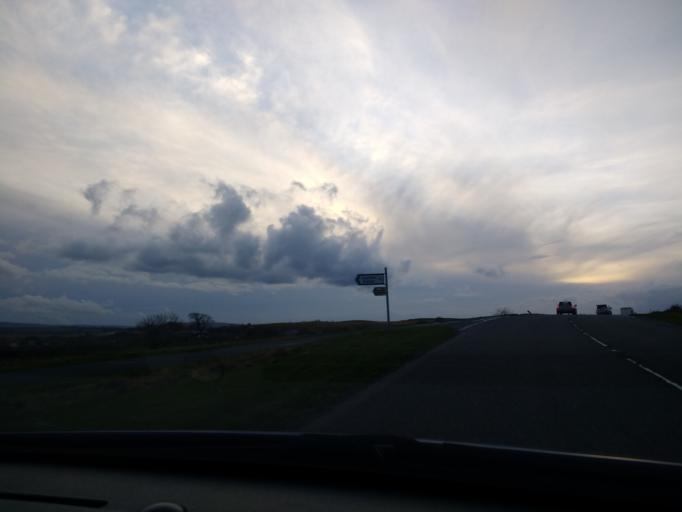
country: GB
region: England
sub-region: North Yorkshire
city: Ingleton
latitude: 54.1256
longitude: -2.4322
